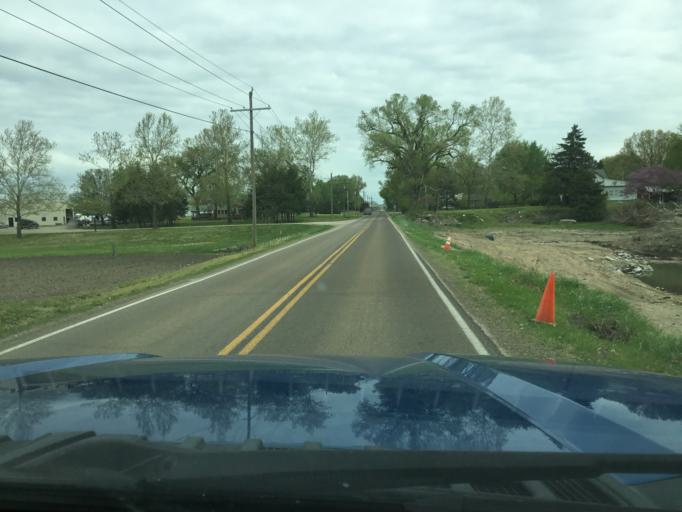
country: US
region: Kansas
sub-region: Douglas County
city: Lawrence
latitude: 38.9881
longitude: -95.2240
